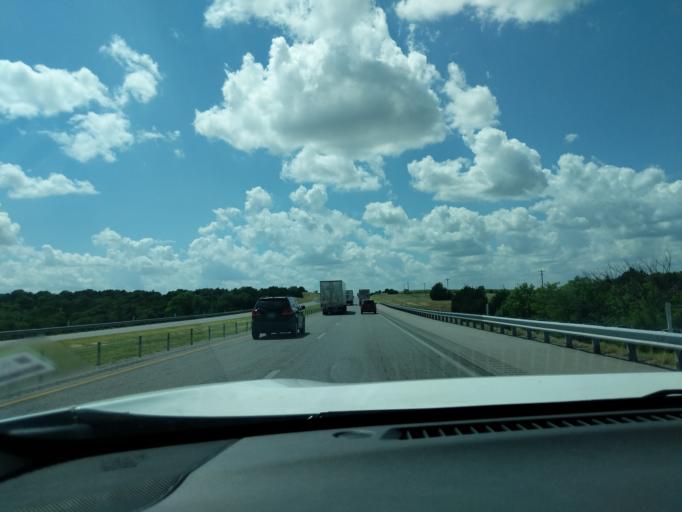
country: US
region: Oklahoma
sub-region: Caddo County
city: Hinton
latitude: 35.5261
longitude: -98.3184
